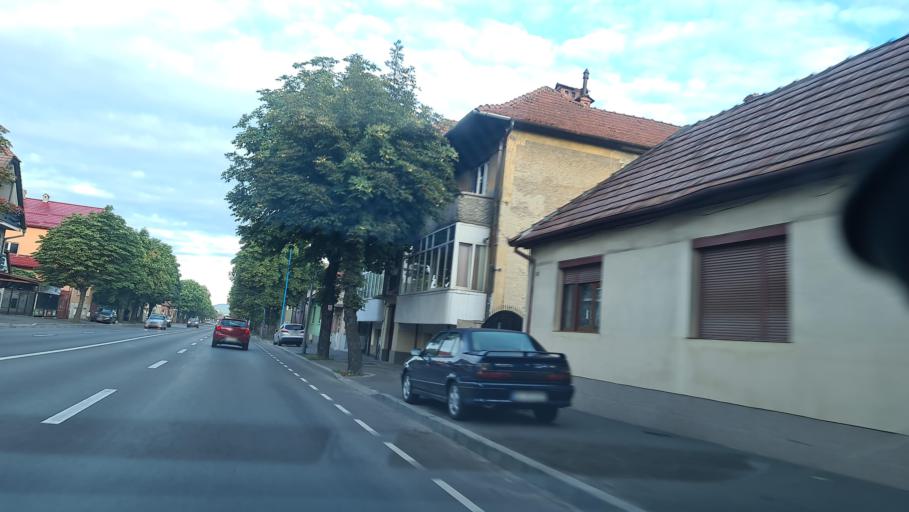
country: RO
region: Brasov
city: Brasov
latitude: 45.6601
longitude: 25.6048
